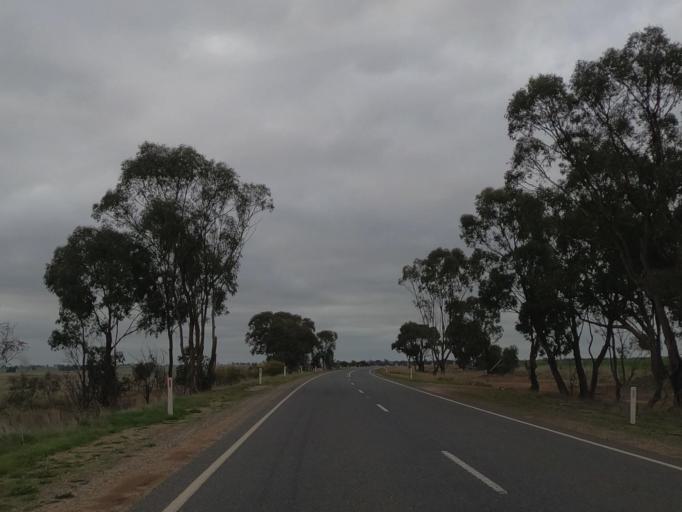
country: AU
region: Victoria
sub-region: Greater Bendigo
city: Long Gully
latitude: -36.5589
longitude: 143.9355
